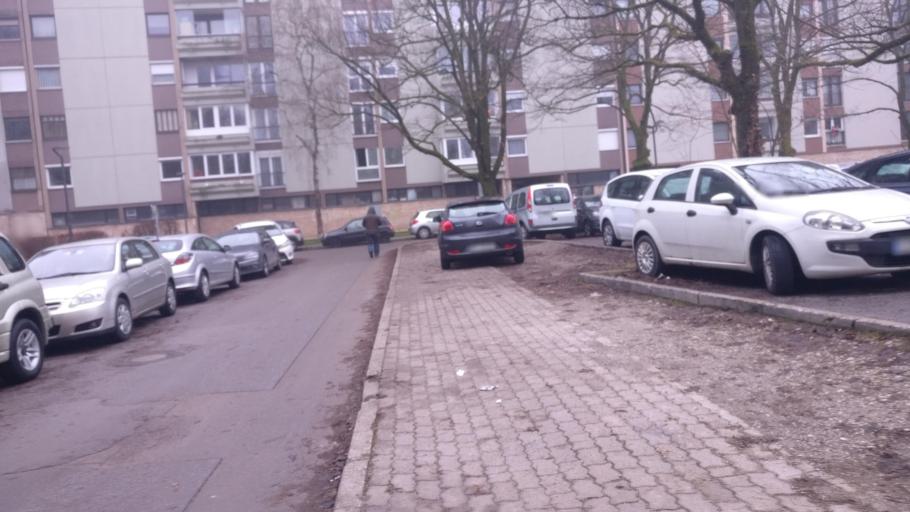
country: SI
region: Ljubljana
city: Ljubljana
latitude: 46.0425
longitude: 14.5037
